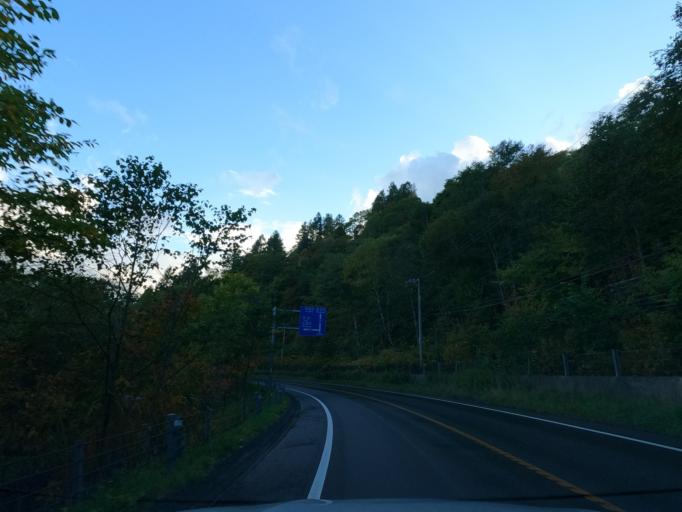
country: JP
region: Hokkaido
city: Shiraoi
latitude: 42.6983
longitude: 141.1064
